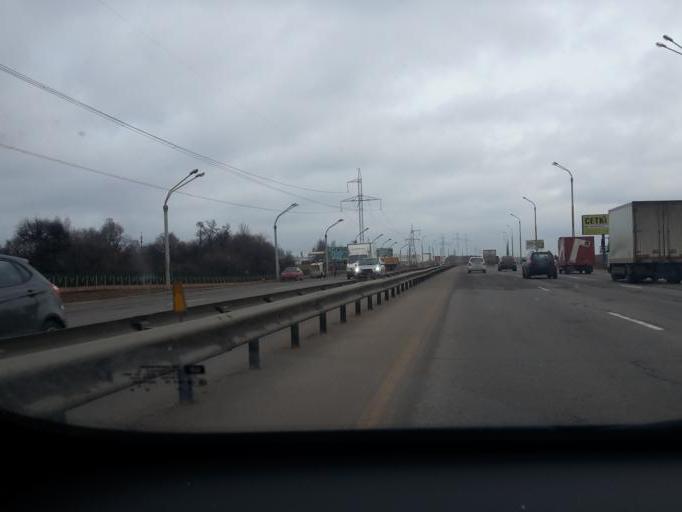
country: BY
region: Minsk
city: Zhdanovichy
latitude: 53.9251
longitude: 27.4172
